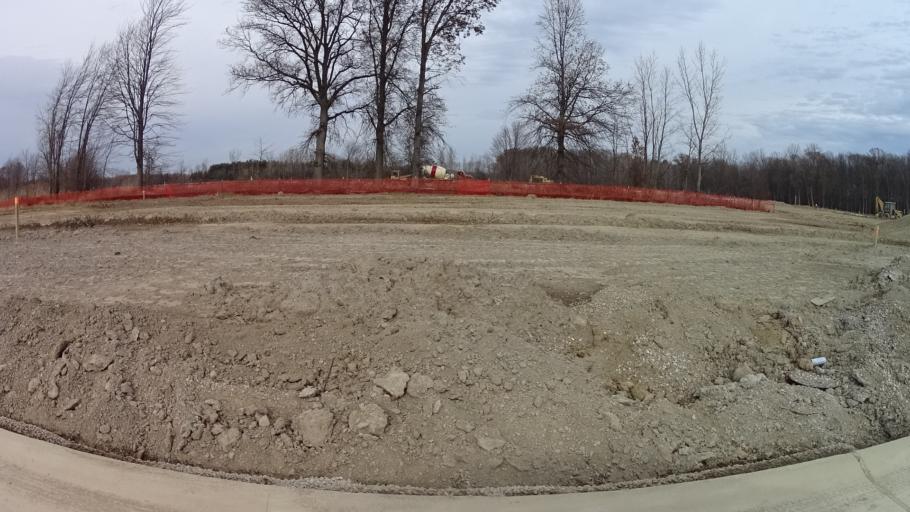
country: US
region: Ohio
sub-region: Lorain County
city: North Ridgeville
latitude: 41.4029
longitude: -82.0290
